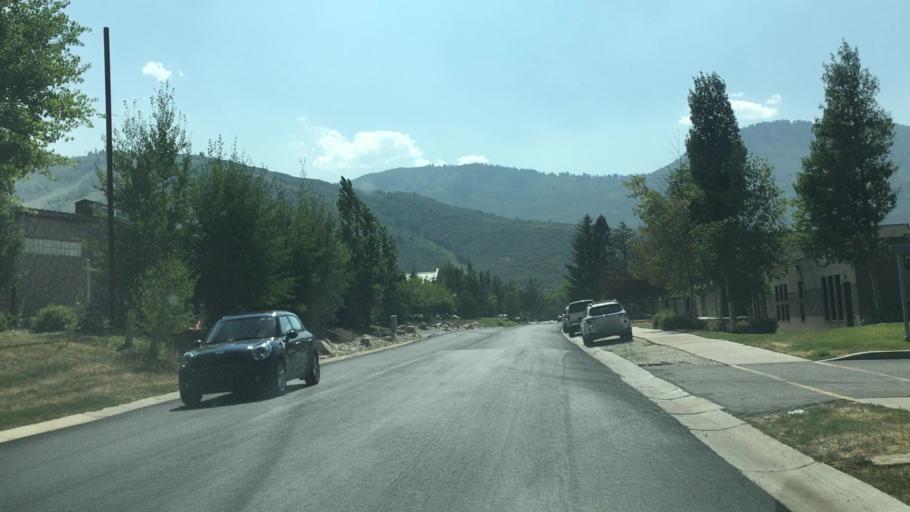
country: US
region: Utah
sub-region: Summit County
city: Park City
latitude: 40.6589
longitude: -111.5032
